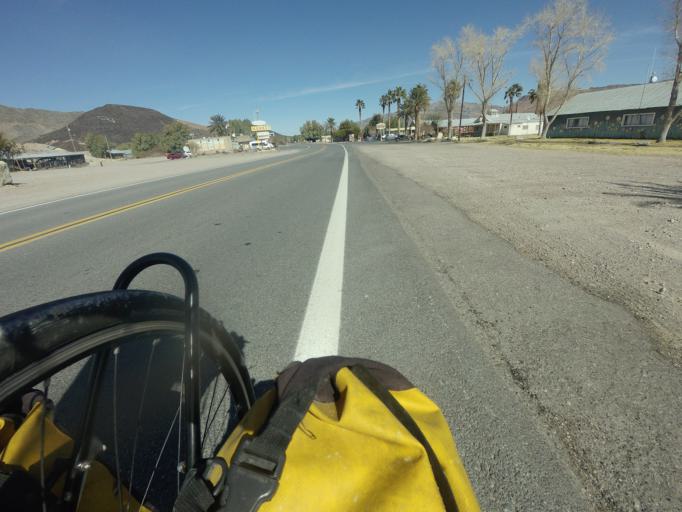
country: US
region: Nevada
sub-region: Nye County
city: Pahrump
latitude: 35.9739
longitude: -116.2703
